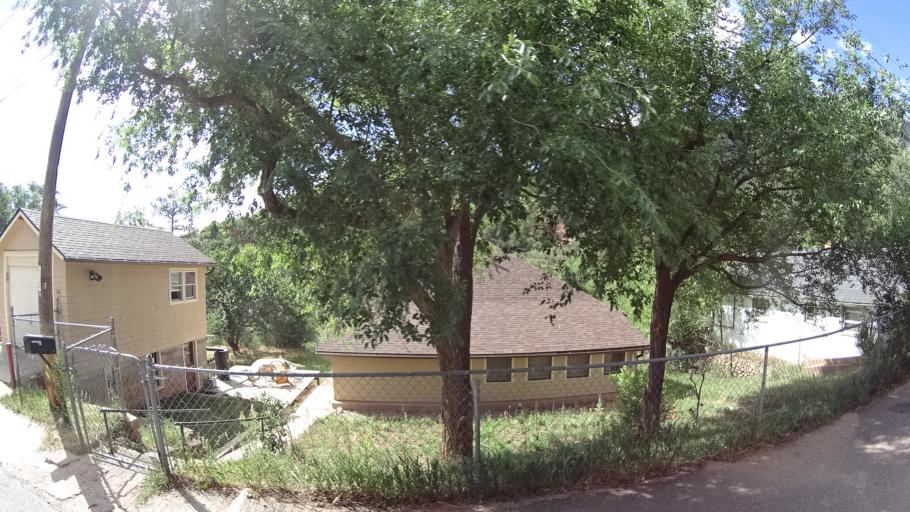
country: US
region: Colorado
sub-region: El Paso County
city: Manitou Springs
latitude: 38.8587
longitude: -104.9259
